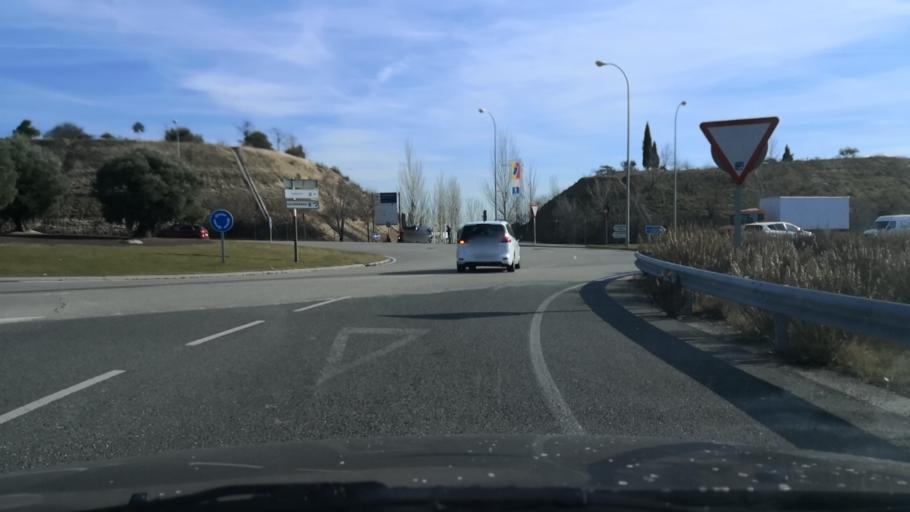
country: ES
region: Madrid
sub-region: Provincia de Madrid
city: Hortaleza
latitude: 40.4719
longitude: -3.6244
